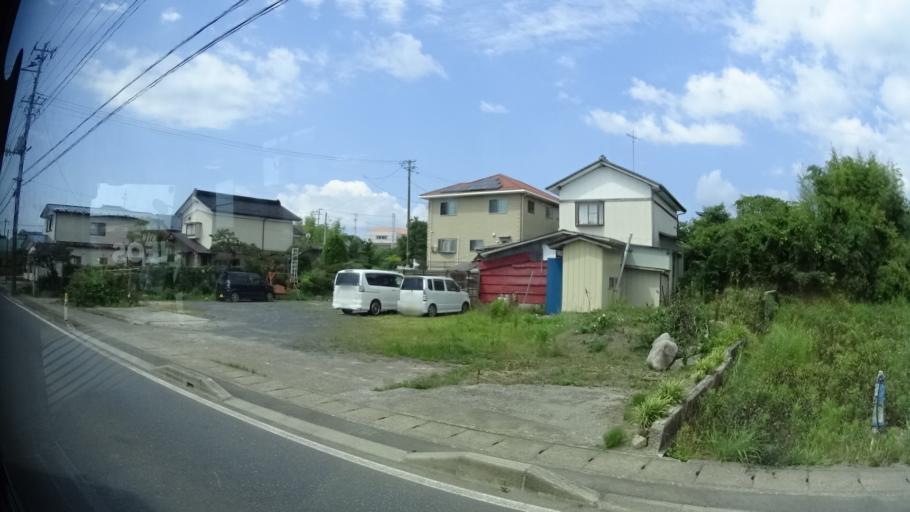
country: JP
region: Iwate
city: Ofunato
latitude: 38.8206
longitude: 141.5730
